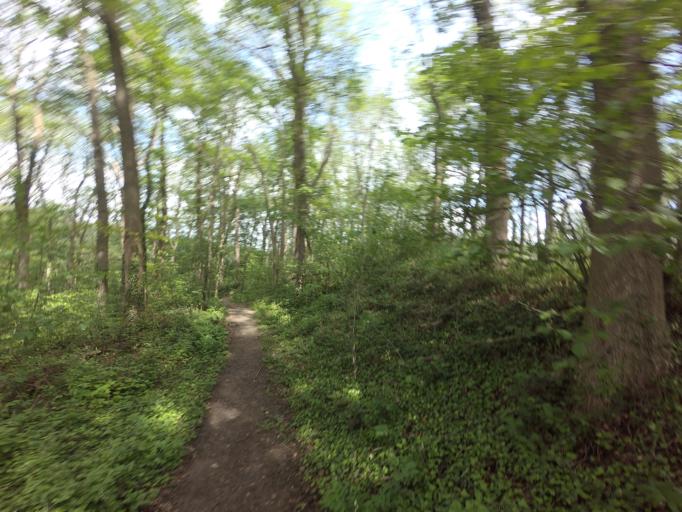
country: NL
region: Limburg
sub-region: Valkenburg aan de Geul
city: Berg
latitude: 50.8375
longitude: 5.7726
